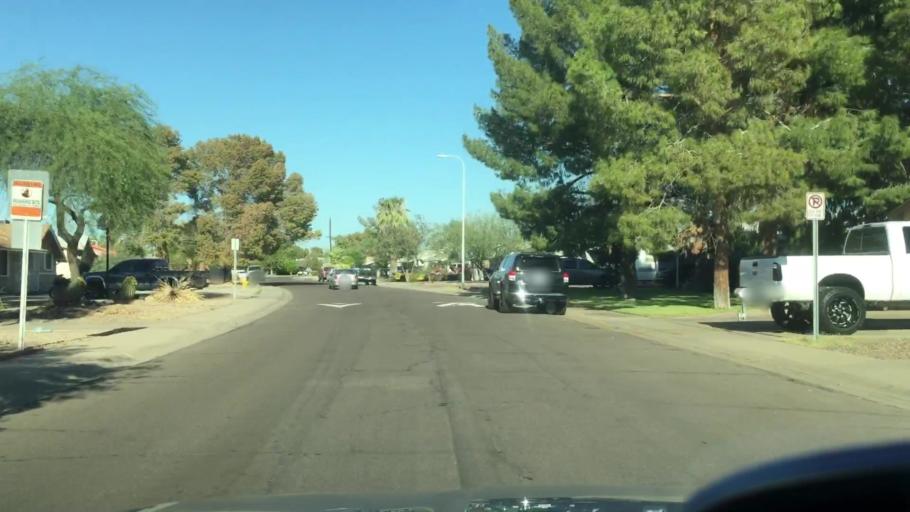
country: US
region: Arizona
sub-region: Maricopa County
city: Tempe
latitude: 33.4051
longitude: -111.9040
